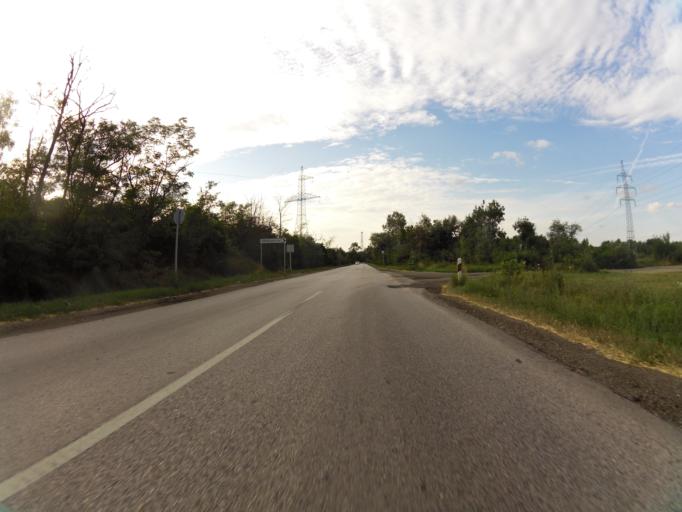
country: HU
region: Csongrad
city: Szeged
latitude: 46.2987
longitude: 20.1332
